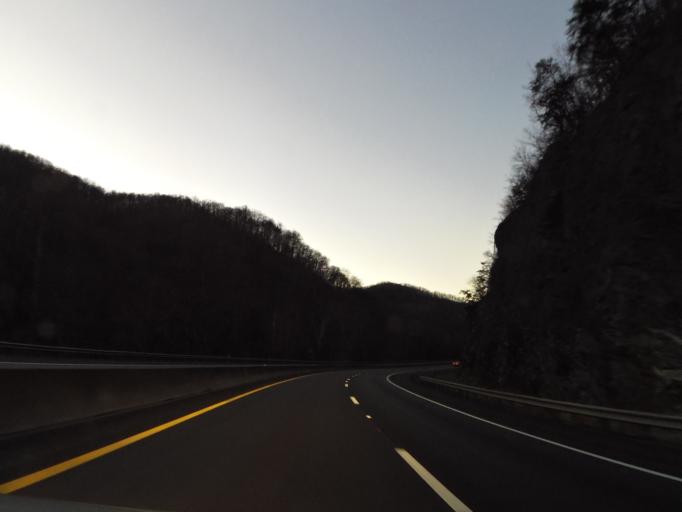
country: US
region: Tennessee
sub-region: Cocke County
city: Newport
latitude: 35.7957
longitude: -83.1283
